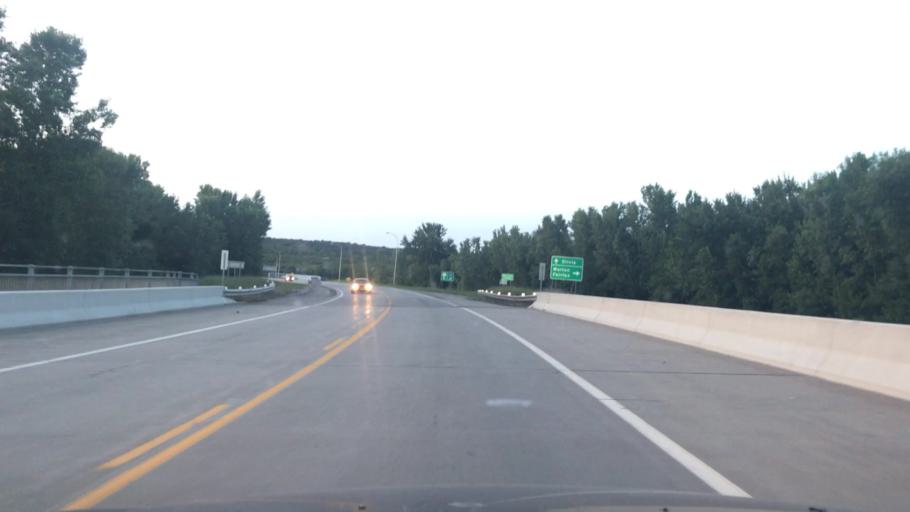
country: US
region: Minnesota
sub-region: Redwood County
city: Redwood Falls
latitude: 44.5458
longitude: -94.9950
